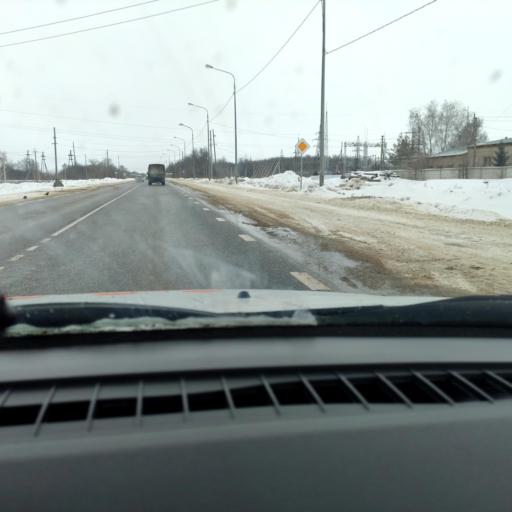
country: RU
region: Samara
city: Dubovyy Umet
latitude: 52.9613
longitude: 50.2920
